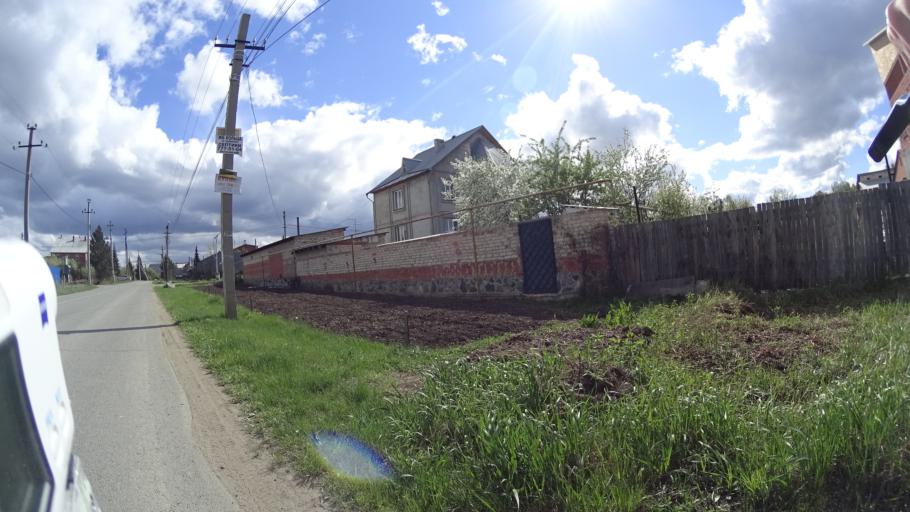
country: RU
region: Chelyabinsk
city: Sargazy
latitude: 55.1495
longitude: 61.2375
